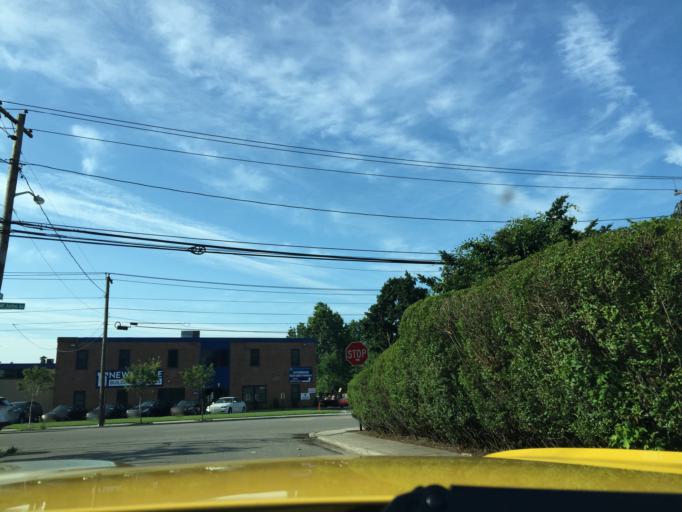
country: US
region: New York
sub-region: Nassau County
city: Hicksville
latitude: 40.7677
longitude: -73.5345
